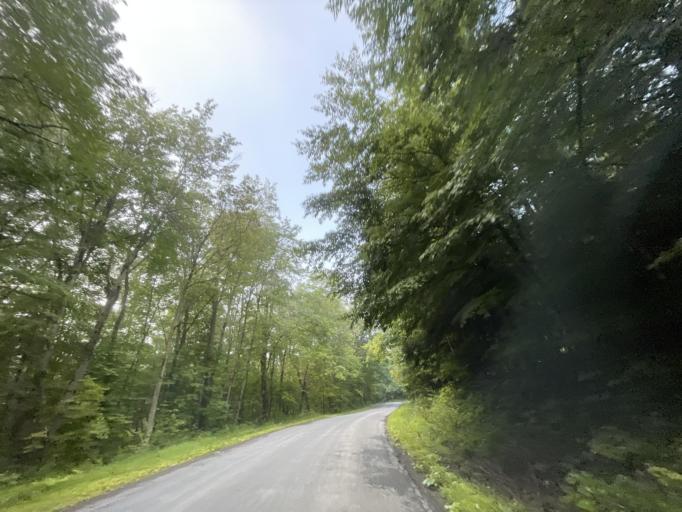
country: US
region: New York
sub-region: Chenango County
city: Oxford
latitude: 42.3922
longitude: -75.6166
